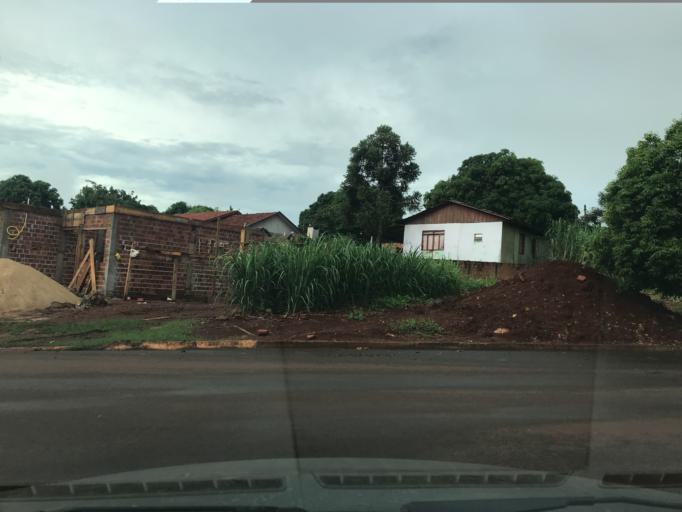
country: BR
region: Parana
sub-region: Palotina
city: Palotina
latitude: -24.2931
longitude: -53.8485
